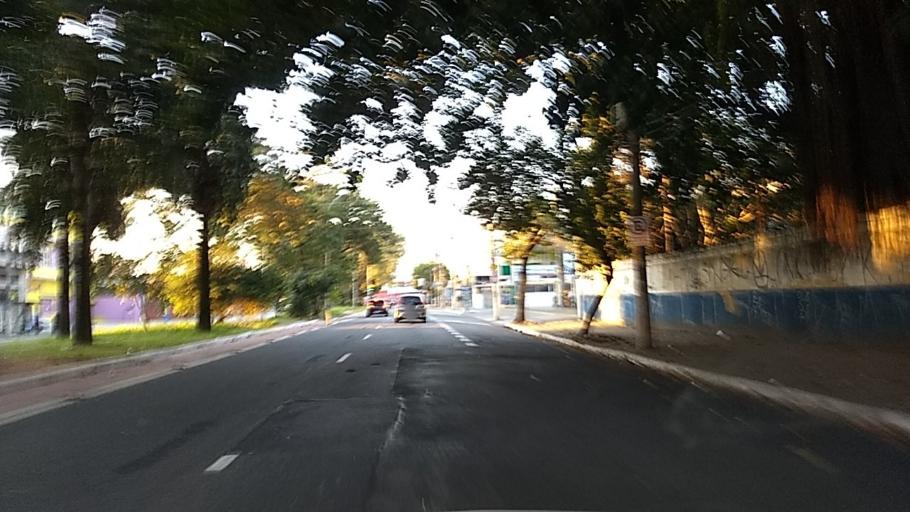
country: BR
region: Sao Paulo
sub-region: Sao Paulo
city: Sao Paulo
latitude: -23.5128
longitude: -46.6066
